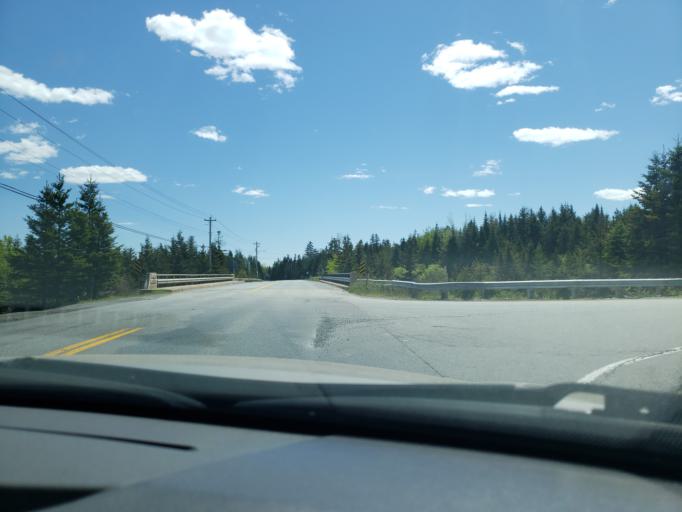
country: CA
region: Nova Scotia
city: Cole Harbour
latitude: 44.7264
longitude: -63.3066
